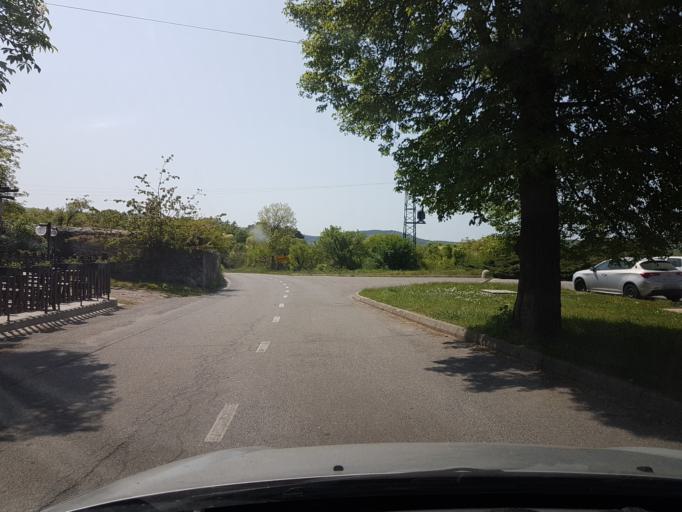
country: SI
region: Komen
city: Komen
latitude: 45.8017
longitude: 13.7110
